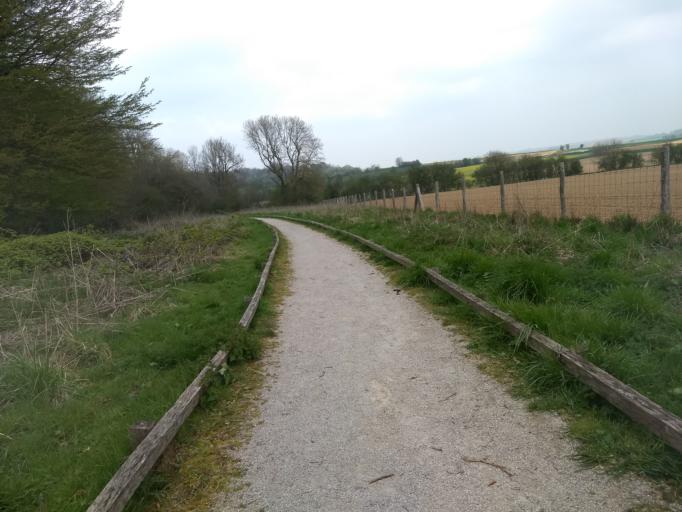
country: FR
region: Nord-Pas-de-Calais
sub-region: Departement du Pas-de-Calais
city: Maroeuil
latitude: 50.3367
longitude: 2.7005
